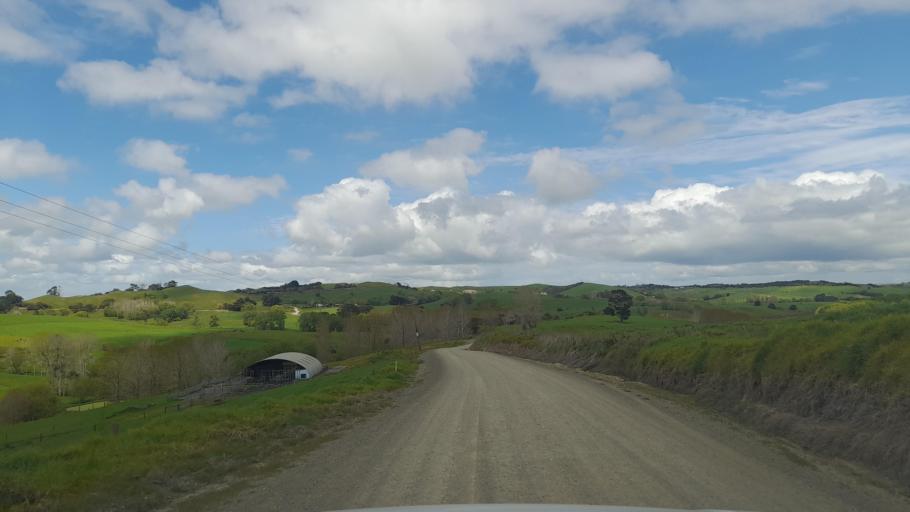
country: NZ
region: Auckland
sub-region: Auckland
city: Wellsford
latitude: -36.1705
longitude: 174.3190
